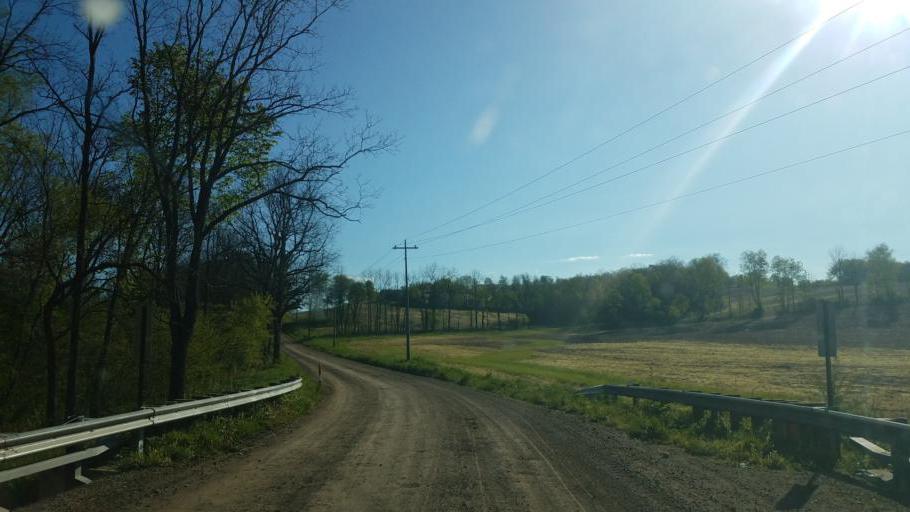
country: US
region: Ohio
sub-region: Knox County
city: Danville
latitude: 40.5466
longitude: -82.3261
